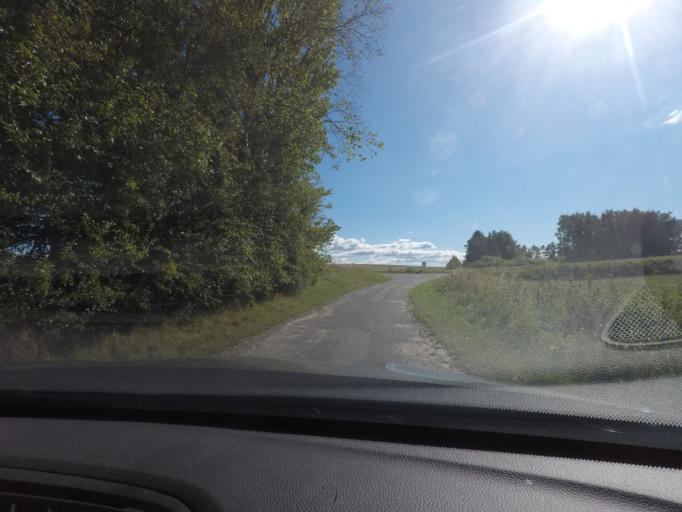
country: DK
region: Zealand
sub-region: Guldborgsund Kommune
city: Sakskobing
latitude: 54.9765
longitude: 11.5487
